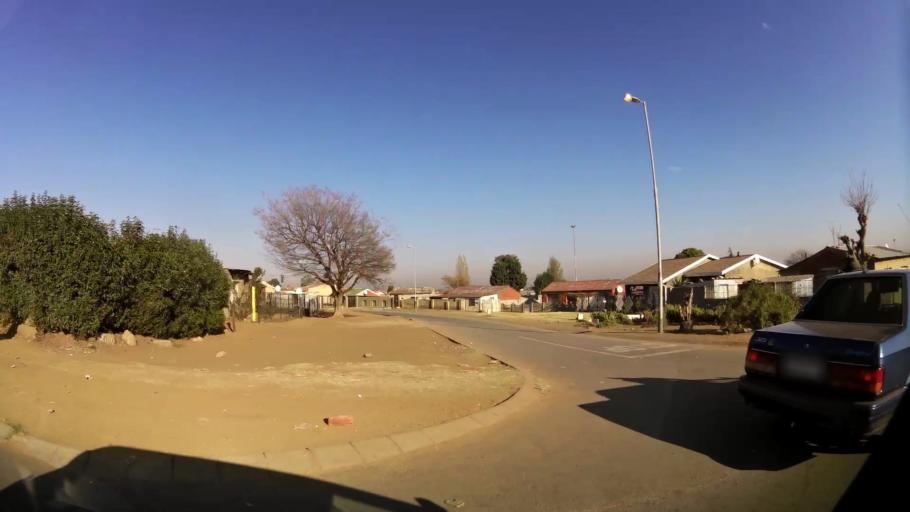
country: ZA
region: Gauteng
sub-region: City of Johannesburg Metropolitan Municipality
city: Soweto
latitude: -26.2345
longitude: 27.9331
